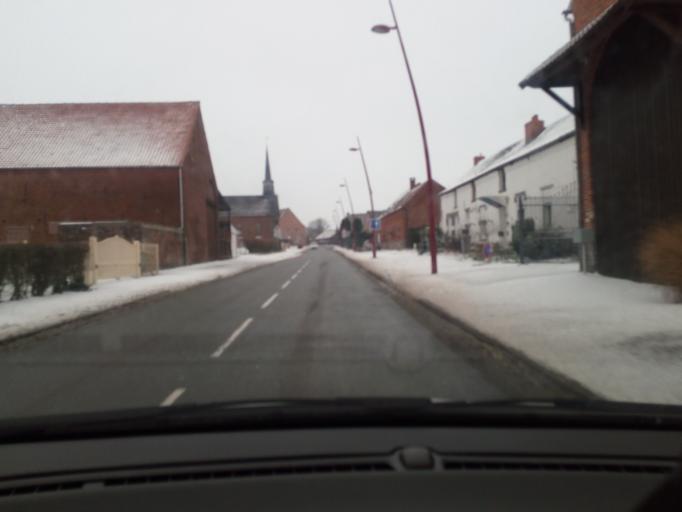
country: FR
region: Nord-Pas-de-Calais
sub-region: Departement du Nord
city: La Longueville
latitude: 50.3245
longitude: 3.8676
